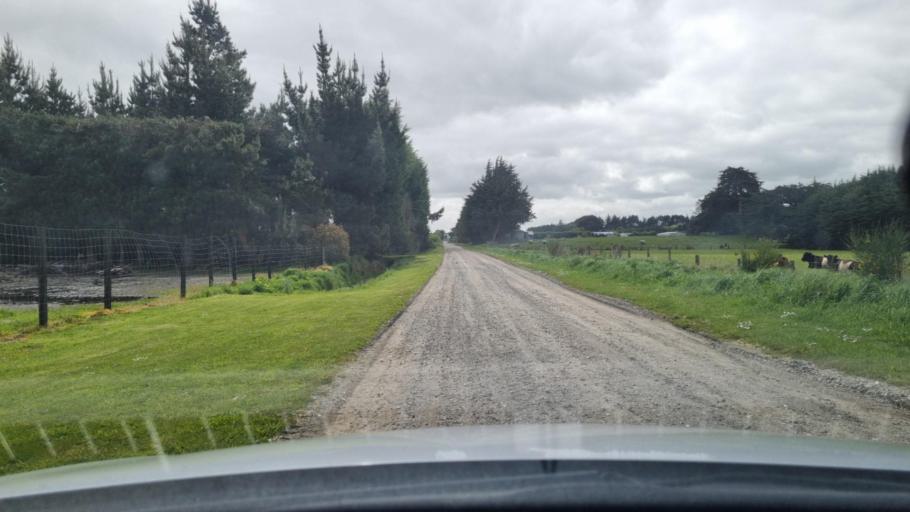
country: NZ
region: Southland
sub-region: Invercargill City
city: Invercargill
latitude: -46.4389
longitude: 168.3896
